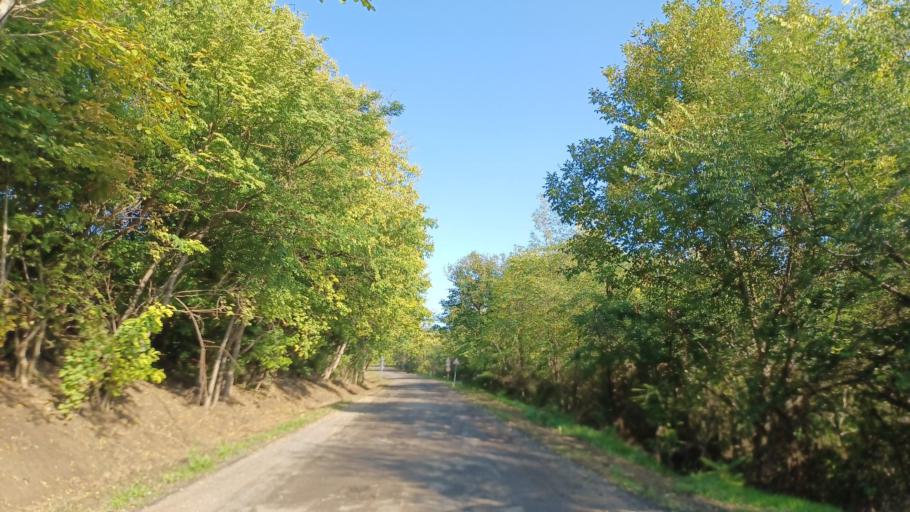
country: HU
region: Tolna
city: Szedres
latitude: 46.5273
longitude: 18.5924
